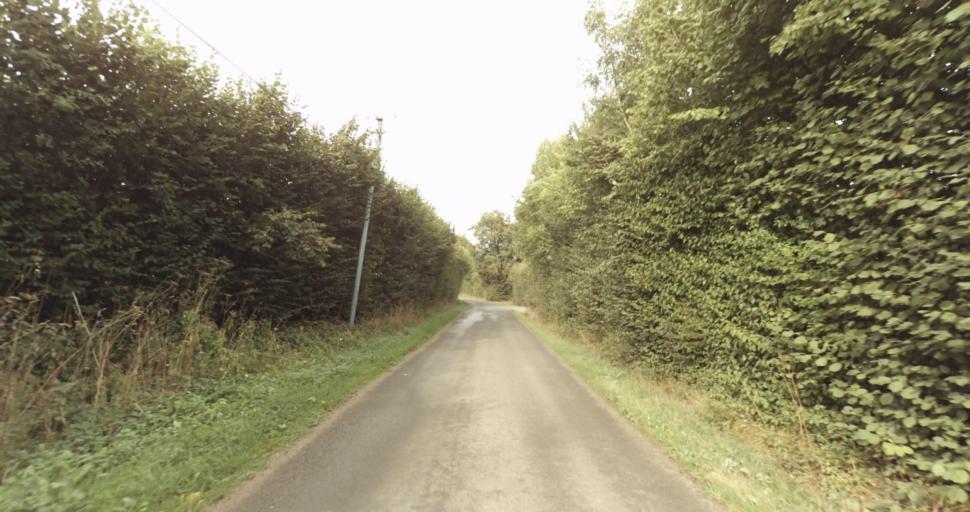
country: FR
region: Lower Normandy
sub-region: Departement de l'Orne
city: Sainte-Gauburge-Sainte-Colombe
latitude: 48.7053
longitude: 0.3701
